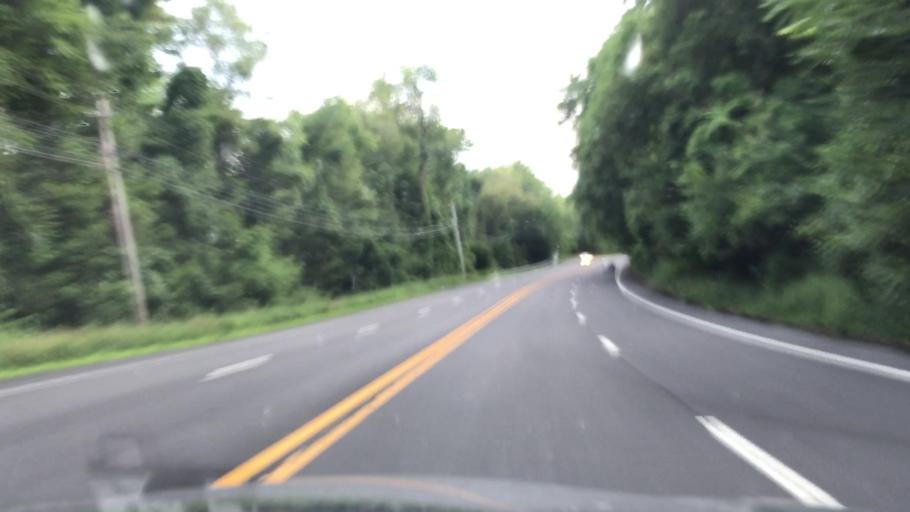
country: US
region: New York
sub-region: Orange County
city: Harriman
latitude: 41.2704
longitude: -74.1552
